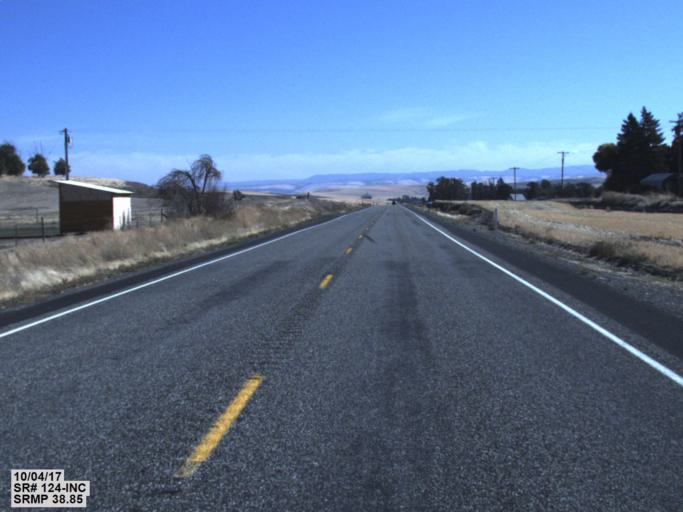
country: US
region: Washington
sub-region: Walla Walla County
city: Waitsburg
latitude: 46.2913
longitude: -118.2607
